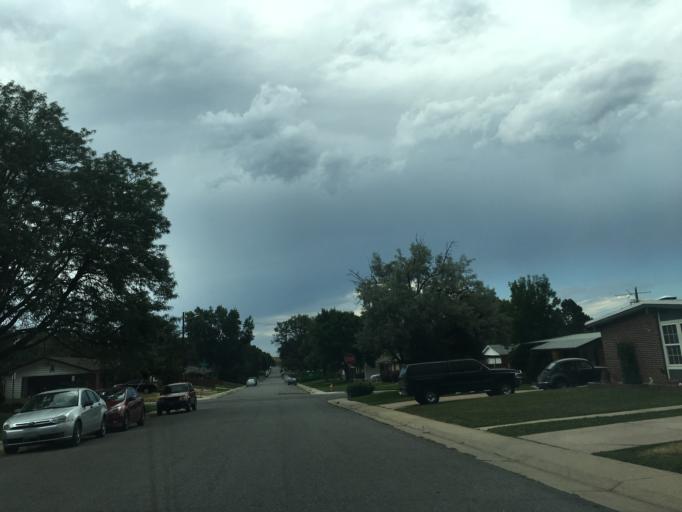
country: US
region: Colorado
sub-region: Arapahoe County
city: Sheridan
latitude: 39.6698
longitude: -105.0397
